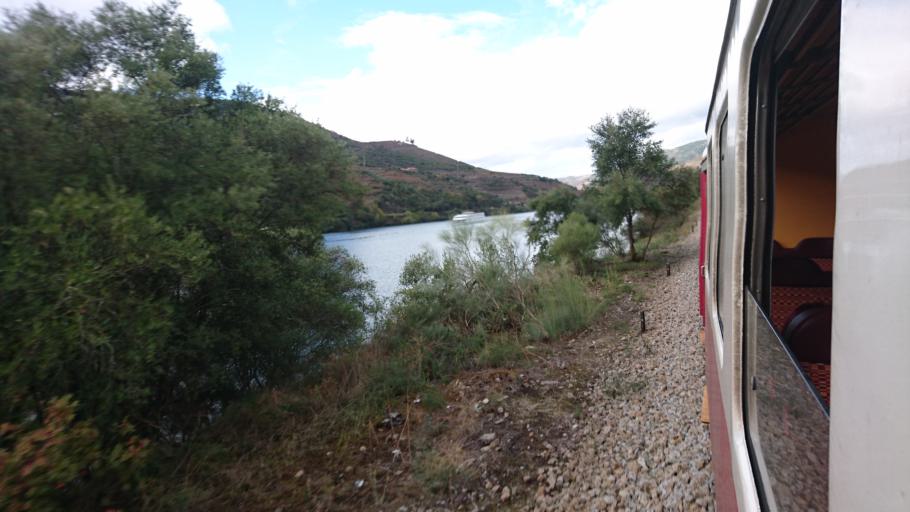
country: PT
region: Viseu
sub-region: Tabuaco
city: Tabuaco
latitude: 41.1579
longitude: -7.5947
